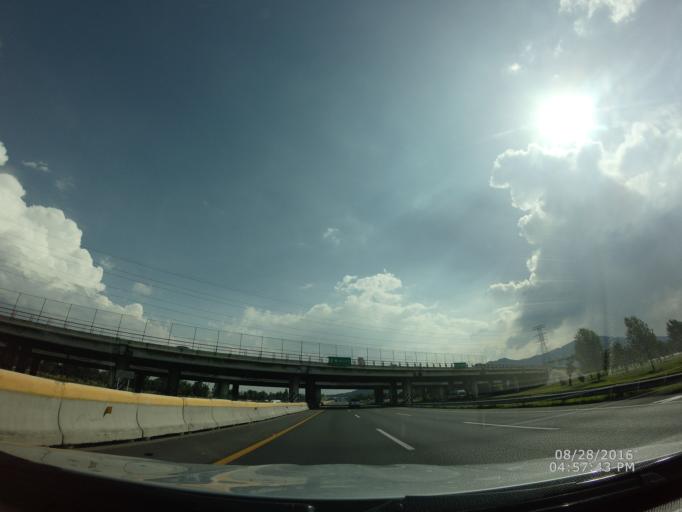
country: MX
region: Mexico
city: Santo Tomas Chiconautla
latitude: 19.6153
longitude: -99.0315
